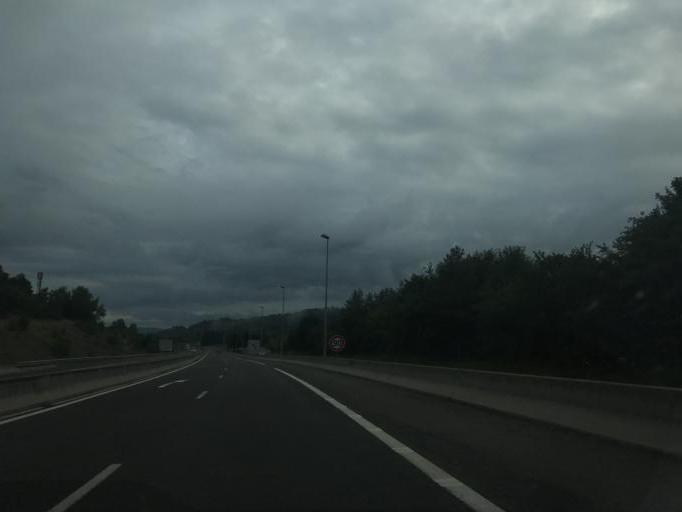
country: FR
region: Rhone-Alpes
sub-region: Departement de l'Ain
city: Oyonnax
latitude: 46.2802
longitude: 5.6595
